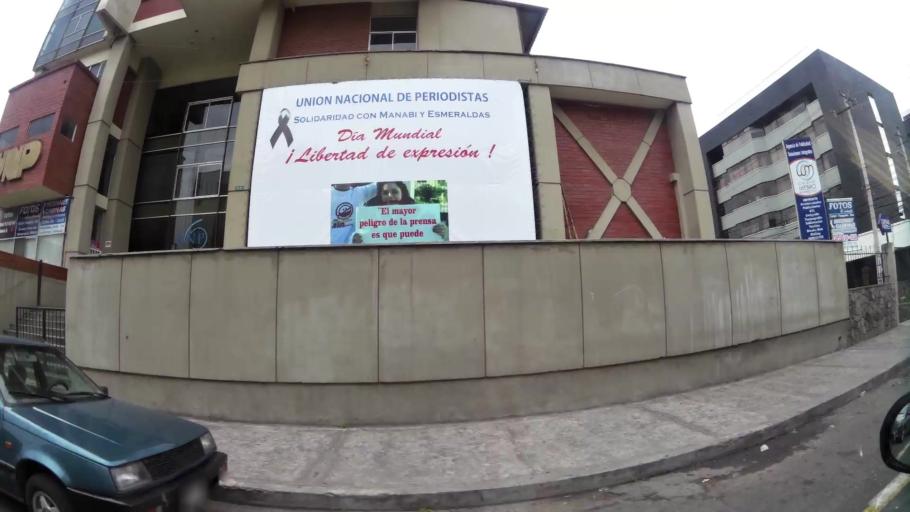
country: EC
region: Pichincha
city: Quito
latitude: -0.1743
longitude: -78.4871
